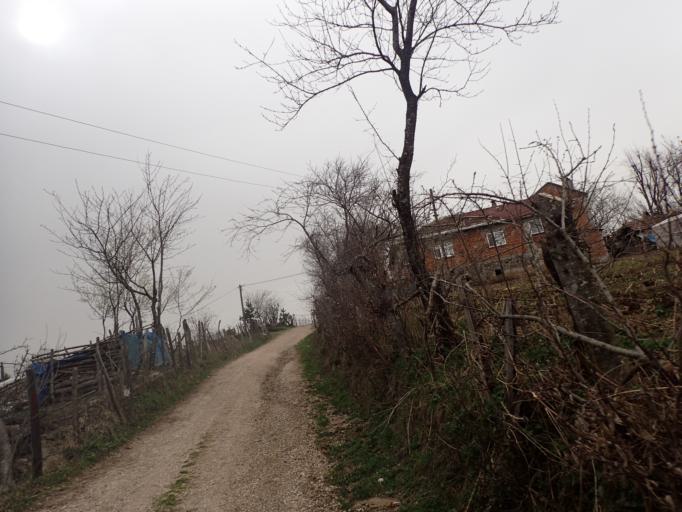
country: TR
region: Ordu
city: Kumru
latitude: 40.8213
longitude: 37.1856
